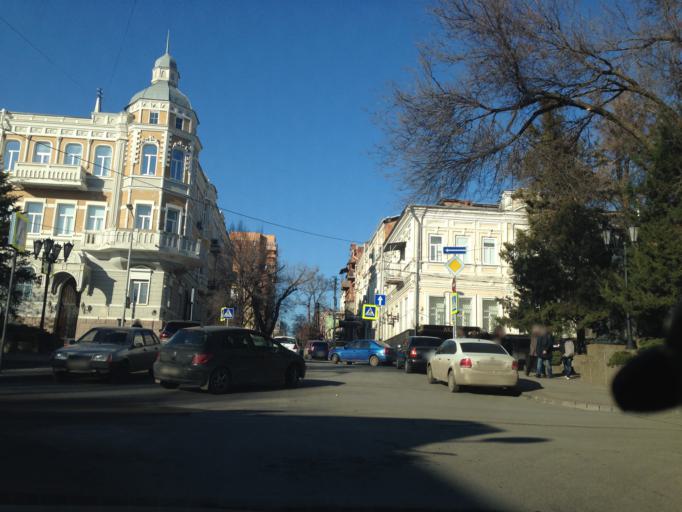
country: RU
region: Rostov
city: Rostov-na-Donu
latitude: 47.2243
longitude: 39.7119
